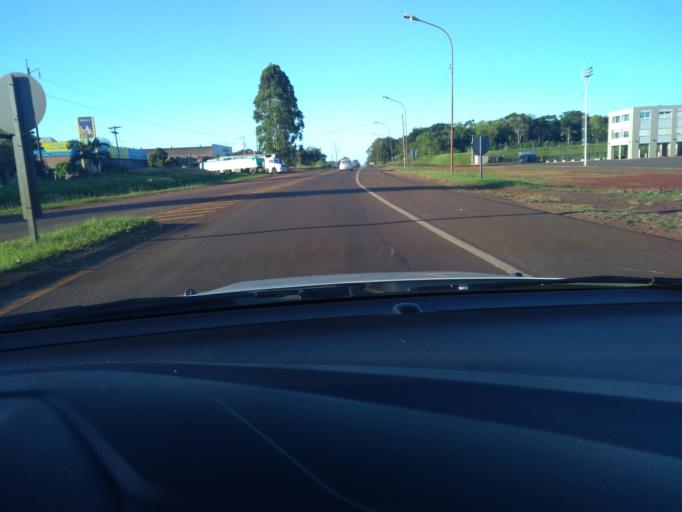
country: AR
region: Misiones
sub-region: Departamento de Obera
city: Obera
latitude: -27.4750
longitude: -55.0864
